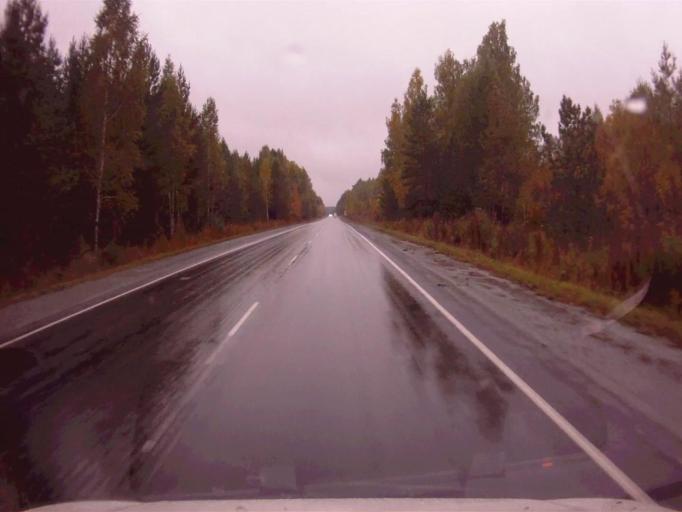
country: RU
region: Chelyabinsk
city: Tayginka
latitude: 55.5416
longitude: 60.6466
